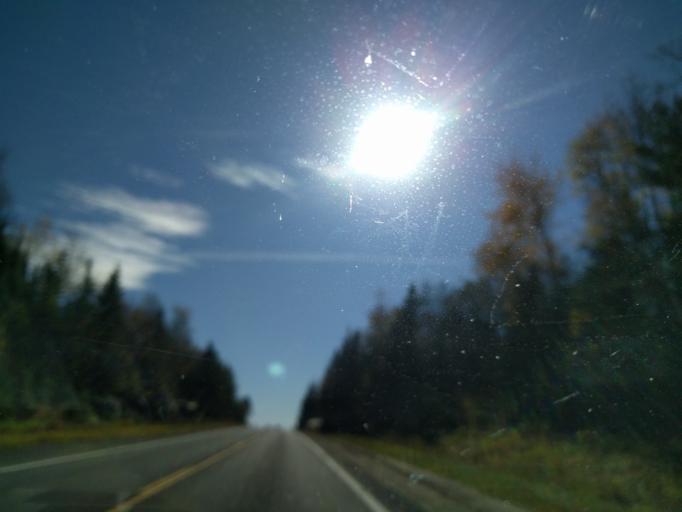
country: US
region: Michigan
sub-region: Marquette County
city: West Ishpeming
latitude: 46.4059
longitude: -87.9976
